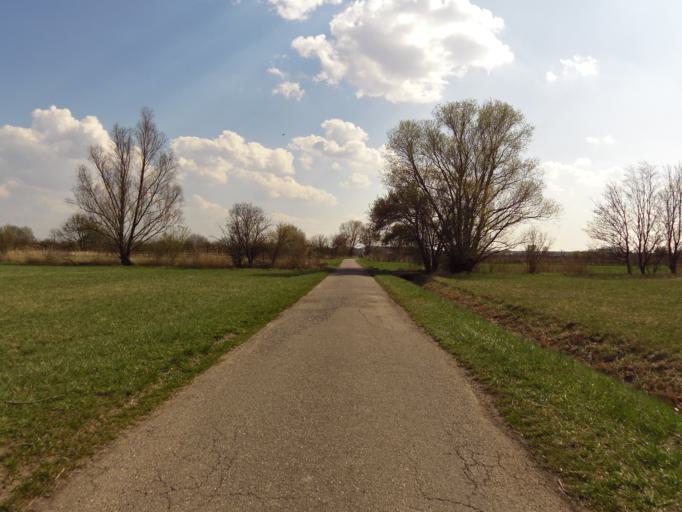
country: DE
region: Rheinland-Pfalz
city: Erpolzheim
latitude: 49.4813
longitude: 8.2039
